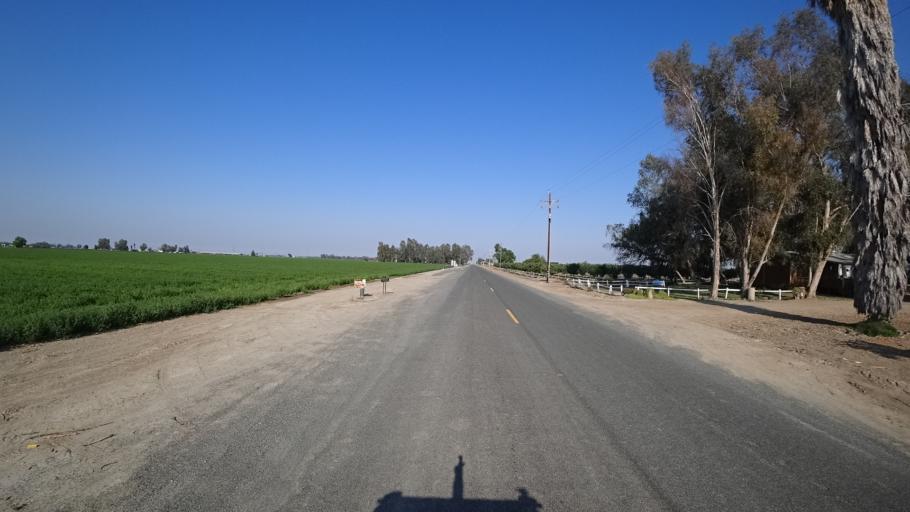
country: US
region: California
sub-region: Fresno County
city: Riverdale
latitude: 36.3584
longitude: -119.8715
